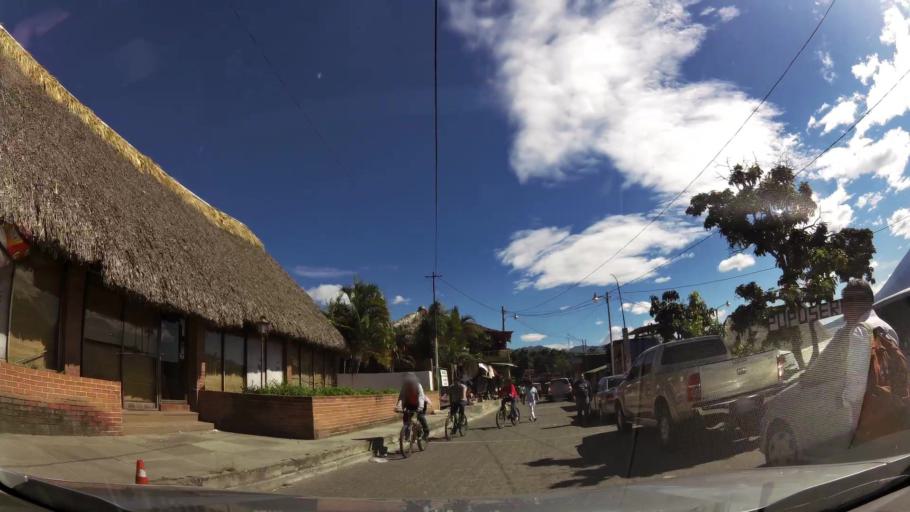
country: GT
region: Solola
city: Panajachel
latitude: 14.7367
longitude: -91.1595
